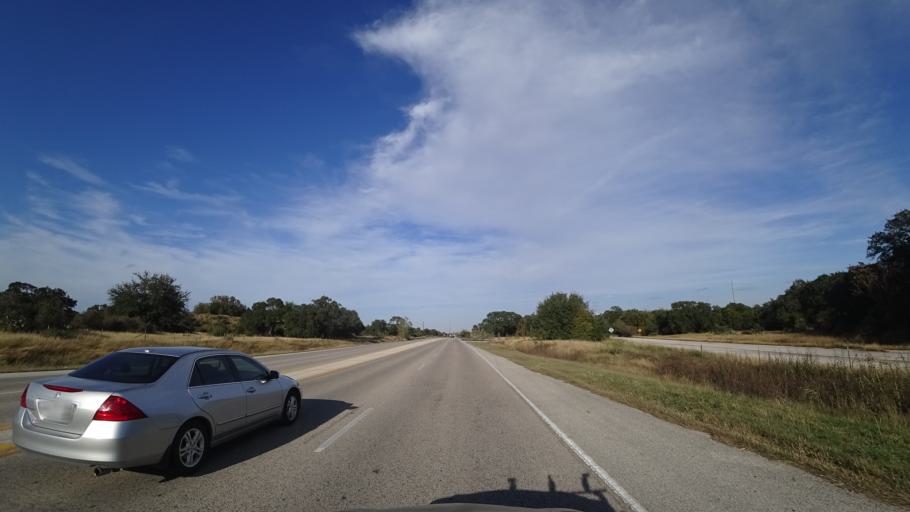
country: US
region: Texas
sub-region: Travis County
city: Wells Branch
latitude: 30.4528
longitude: -97.7246
